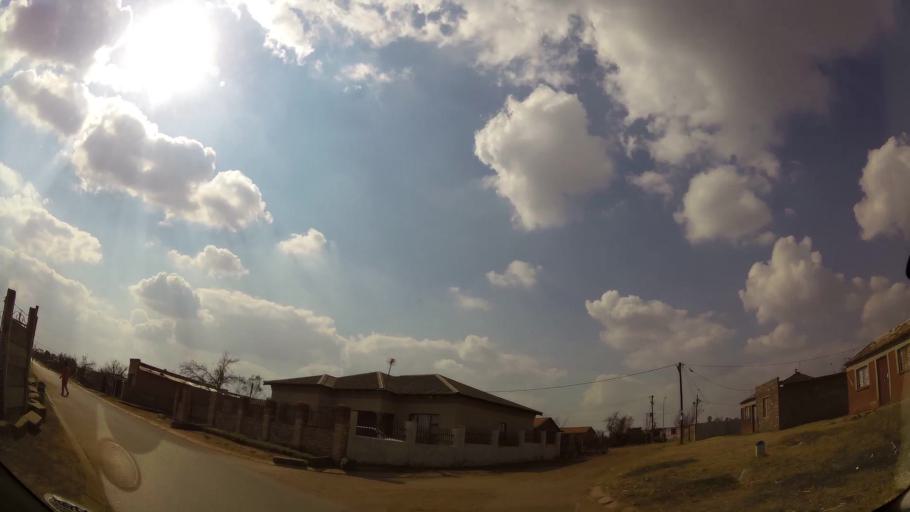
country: ZA
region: Gauteng
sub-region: Ekurhuleni Metropolitan Municipality
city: Springs
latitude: -26.1332
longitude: 28.4762
